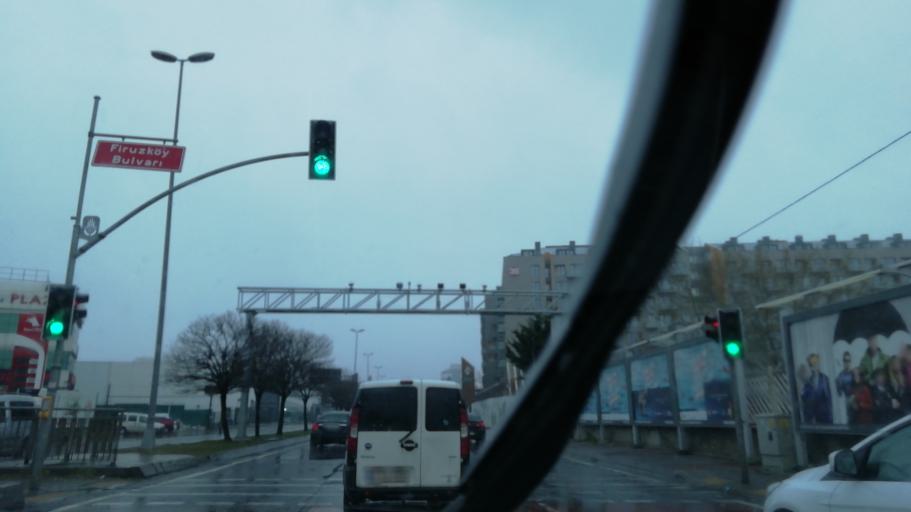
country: TR
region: Istanbul
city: Yakuplu
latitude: 40.9906
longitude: 28.7191
